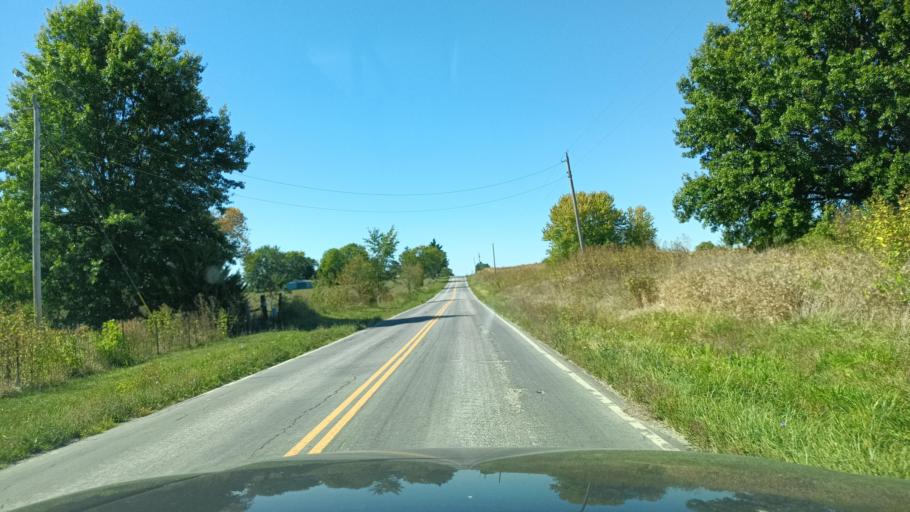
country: US
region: Missouri
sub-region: Macon County
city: La Plata
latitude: 40.0224
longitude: -92.5612
